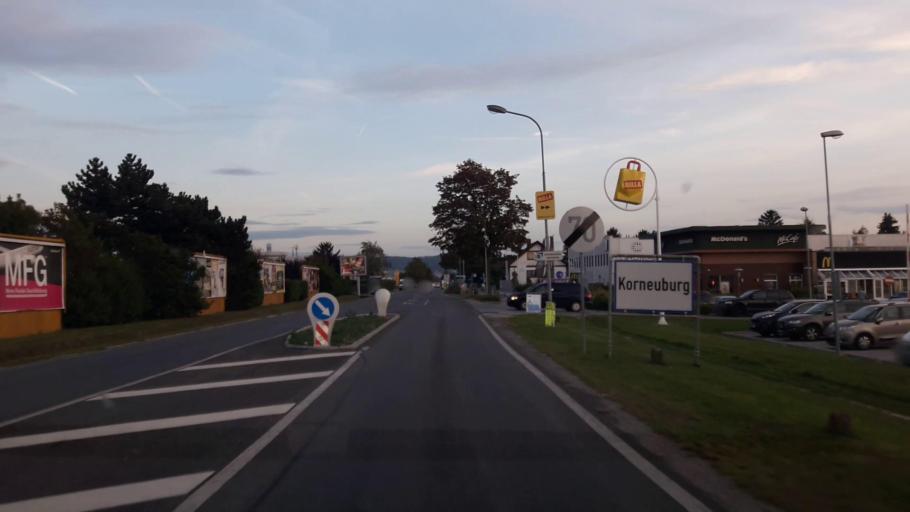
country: AT
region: Lower Austria
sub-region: Politischer Bezirk Korneuburg
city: Korneuburg
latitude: 48.3599
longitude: 16.3120
